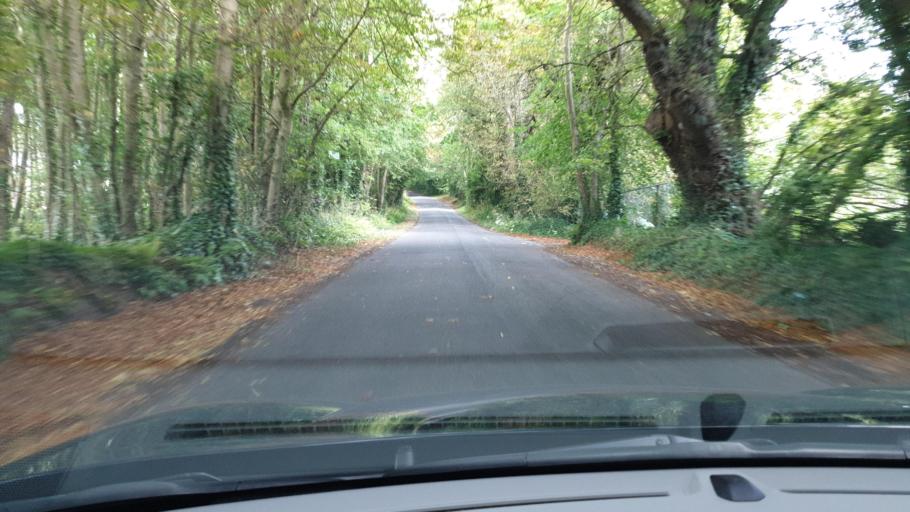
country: IE
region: Leinster
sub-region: Fingal County
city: Skerries
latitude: 53.5676
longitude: -6.1336
